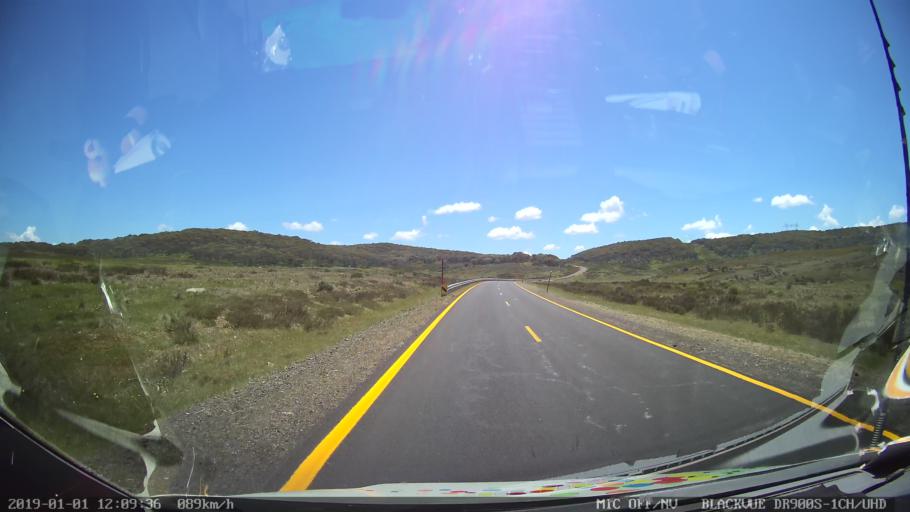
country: AU
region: New South Wales
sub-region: Tumut Shire
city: Tumut
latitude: -35.8052
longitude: 148.4961
